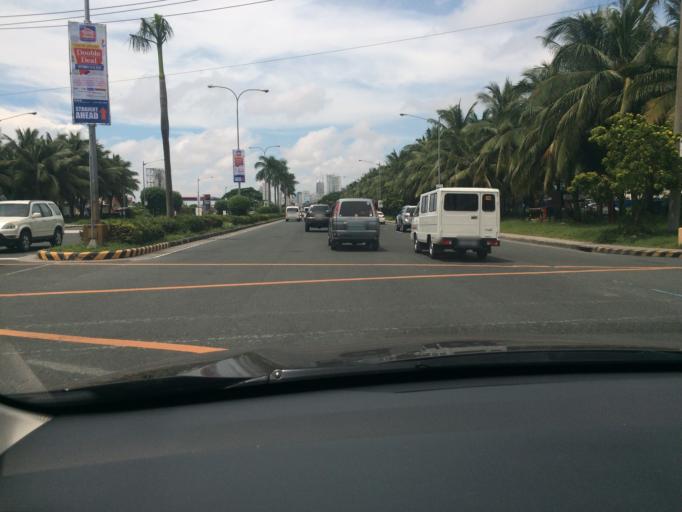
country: PH
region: Metro Manila
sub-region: Makati City
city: Makati City
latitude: 14.5404
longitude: 120.9884
